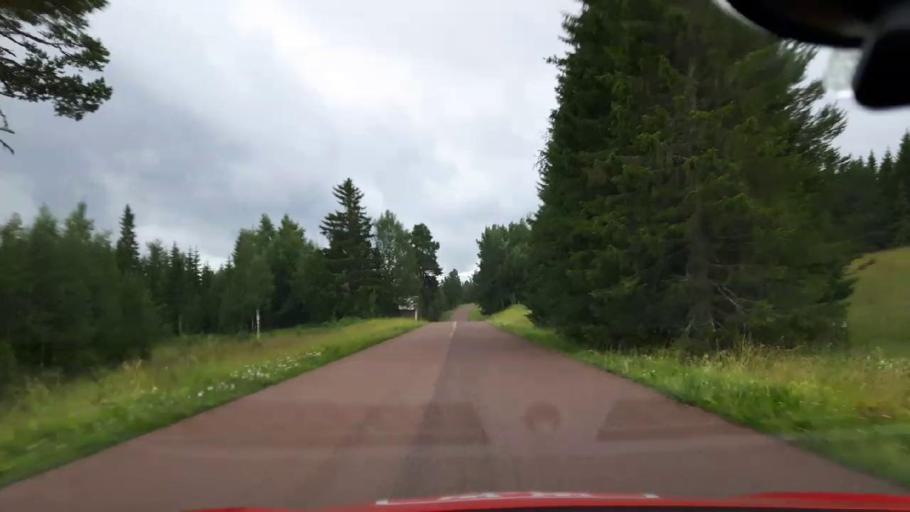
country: SE
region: Jaemtland
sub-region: Krokoms Kommun
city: Valla
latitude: 63.3482
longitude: 13.7223
